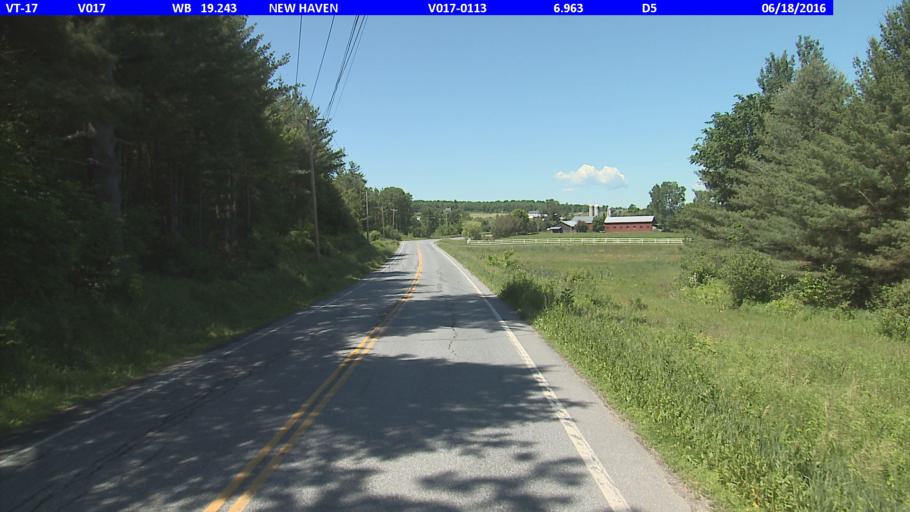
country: US
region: Vermont
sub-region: Addison County
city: Bristol
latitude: 44.1289
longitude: -73.1135
